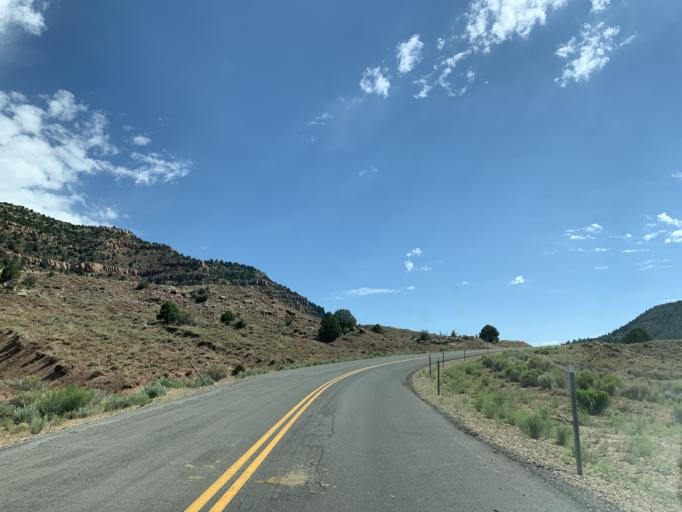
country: US
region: Utah
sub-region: Carbon County
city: East Carbon City
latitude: 39.7410
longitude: -110.5647
